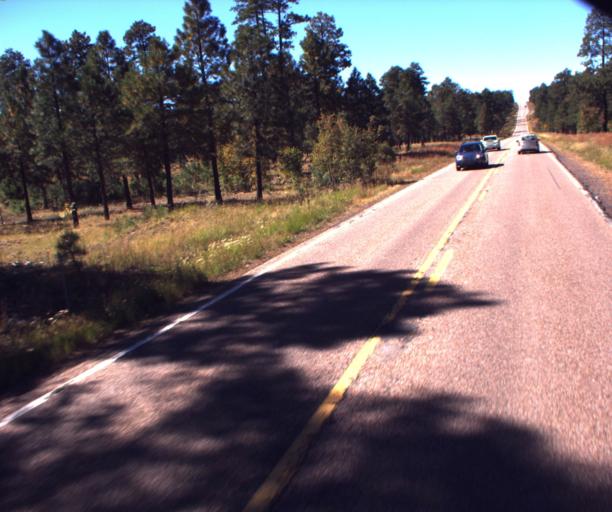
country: US
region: Arizona
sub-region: Navajo County
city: Heber-Overgaard
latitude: 34.3376
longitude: -110.7342
